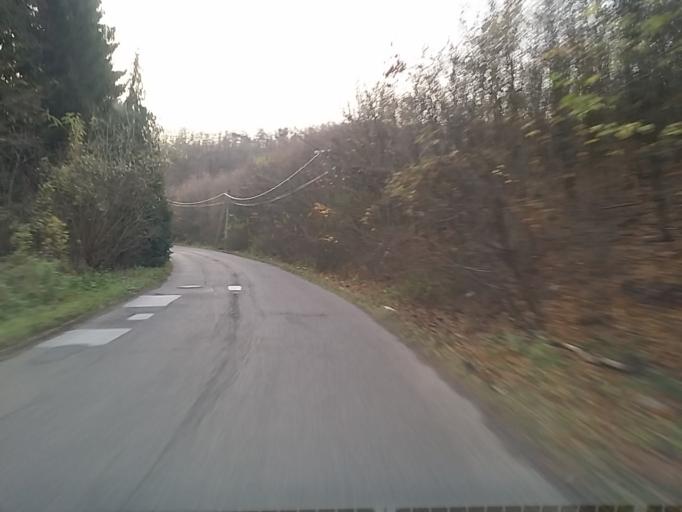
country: HU
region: Heves
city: Abasar
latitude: 47.8168
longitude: 19.9847
